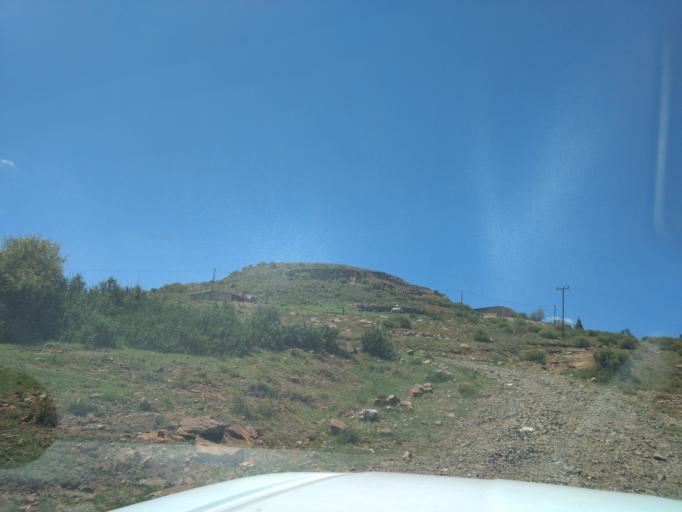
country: LS
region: Maseru
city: Maseru
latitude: -29.4570
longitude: 27.3752
